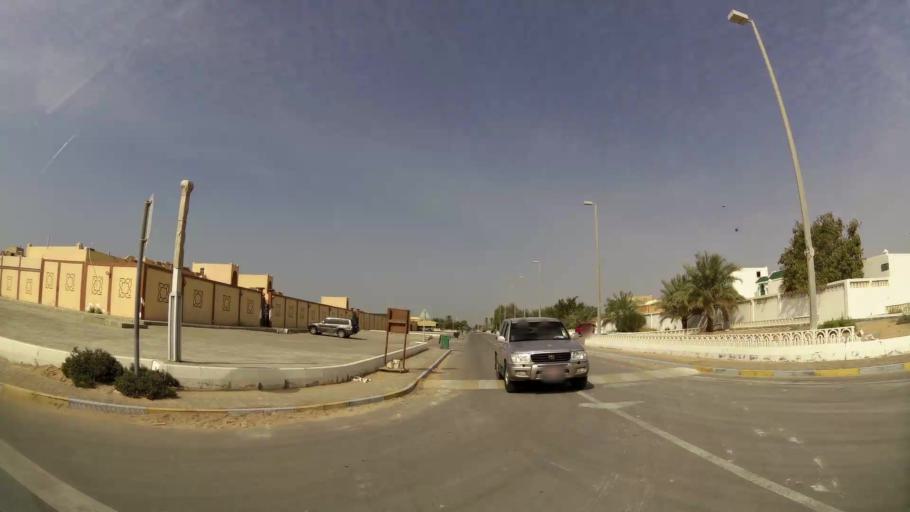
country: AE
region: Abu Dhabi
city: Abu Dhabi
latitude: 24.5923
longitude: 54.6954
